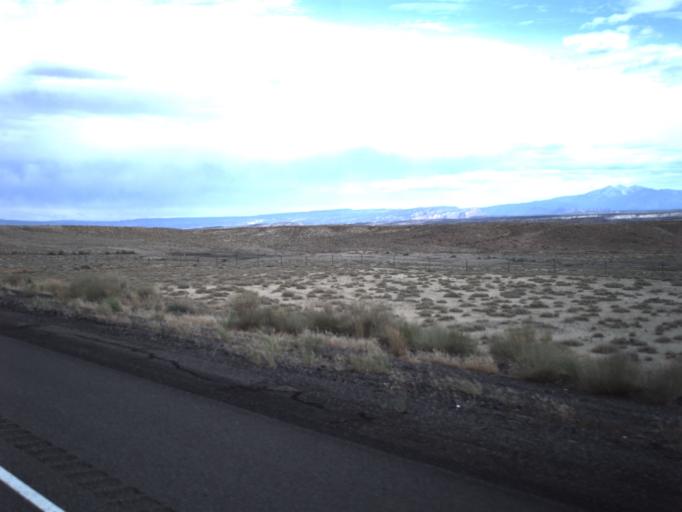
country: US
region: Utah
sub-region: Grand County
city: Moab
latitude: 38.9385
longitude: -109.4997
